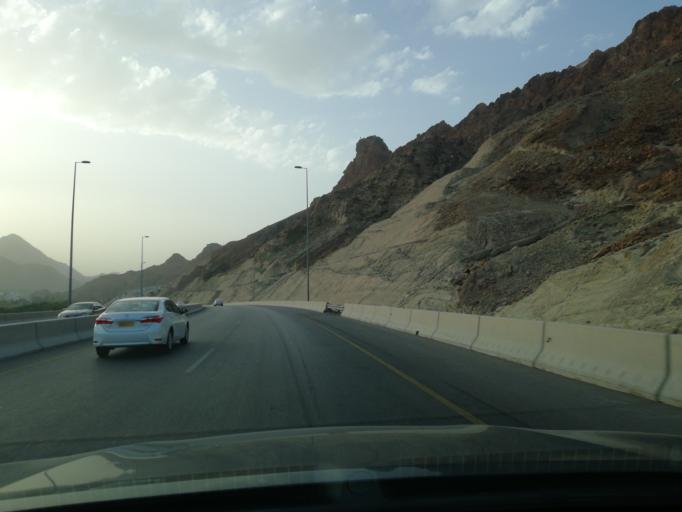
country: OM
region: Muhafazat ad Dakhiliyah
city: Bidbid
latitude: 23.4513
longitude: 58.1220
